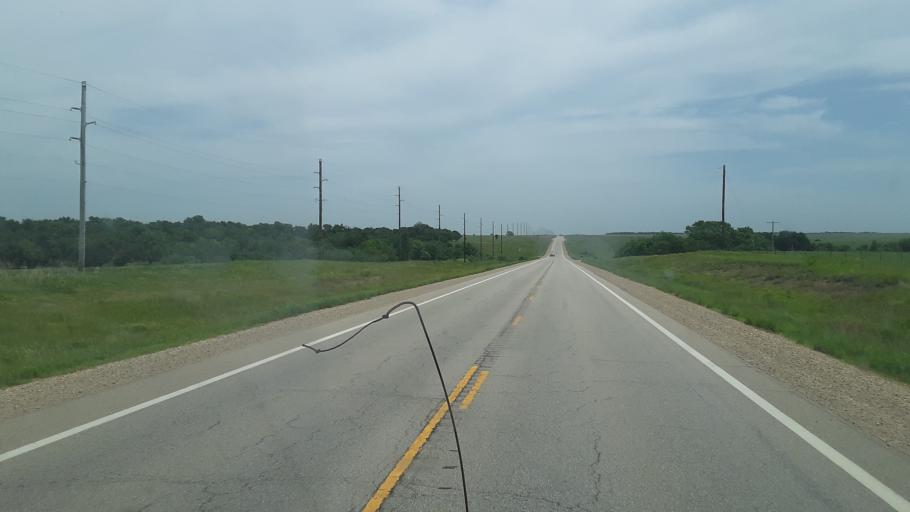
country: US
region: Kansas
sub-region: Greenwood County
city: Eureka
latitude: 37.8372
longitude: -96.0432
